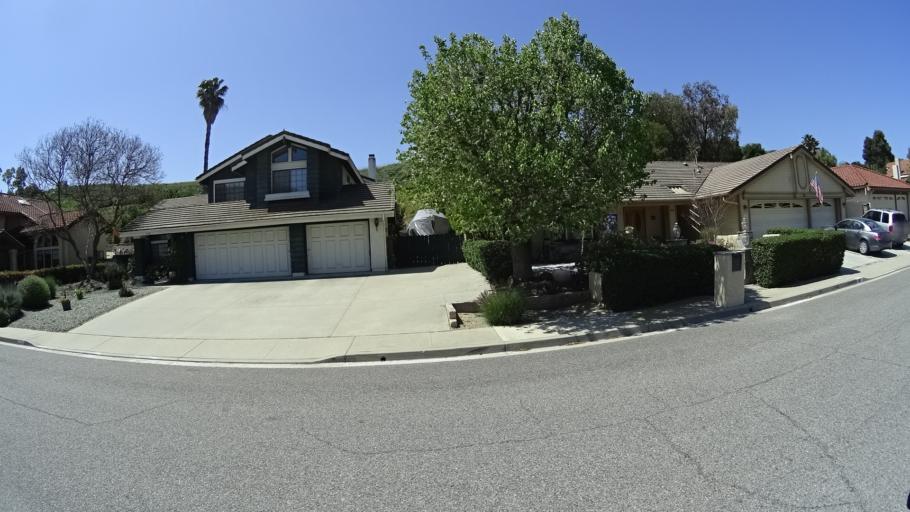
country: US
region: California
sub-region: Ventura County
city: Casa Conejo
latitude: 34.2044
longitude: -118.8984
